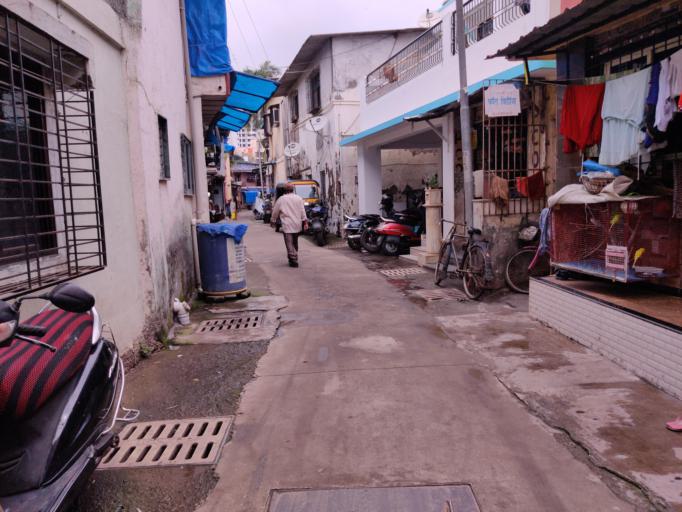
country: IN
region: Maharashtra
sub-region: Mumbai Suburban
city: Borivli
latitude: 19.2569
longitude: 72.8574
